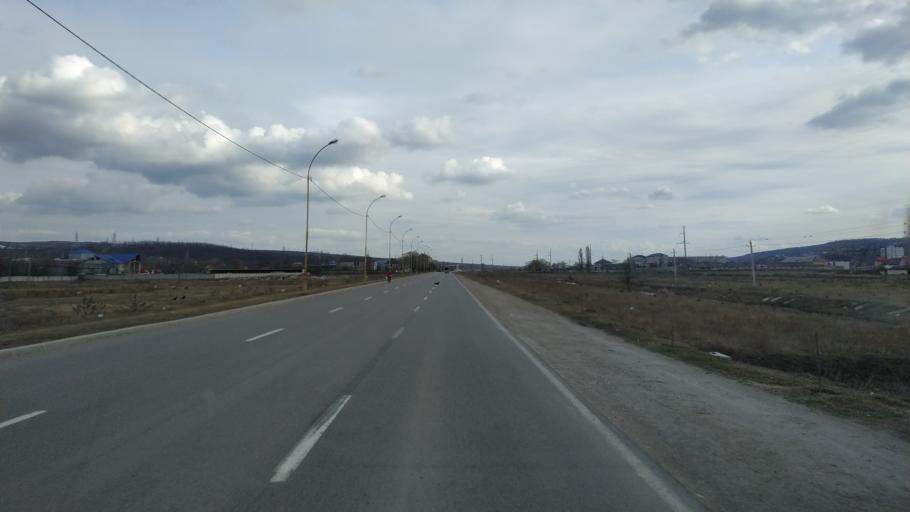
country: MD
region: Hincesti
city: Hincesti
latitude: 46.8292
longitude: 28.6007
